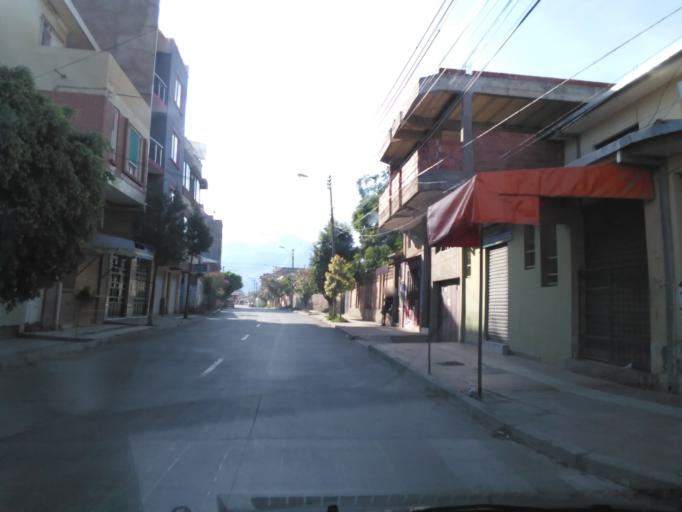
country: BO
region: Cochabamba
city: Cochabamba
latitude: -17.3387
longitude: -66.2161
